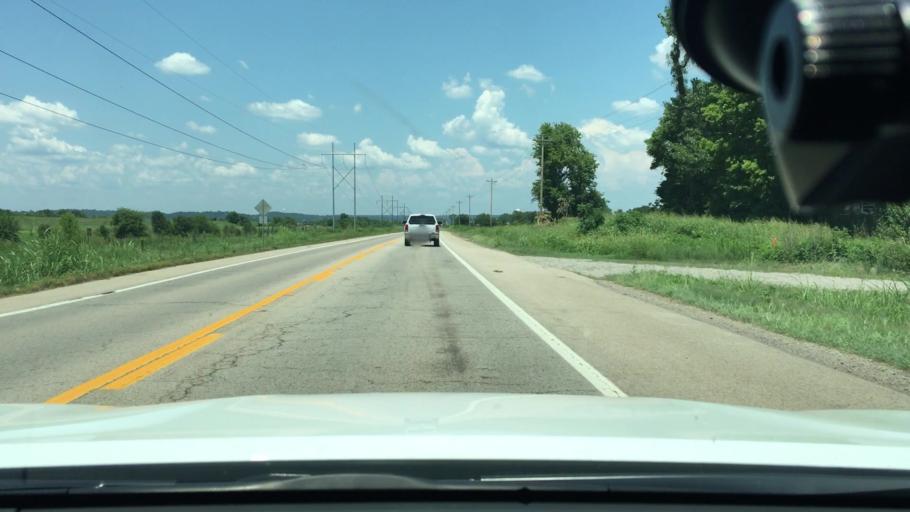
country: US
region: Arkansas
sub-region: Crawford County
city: Van Buren
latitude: 35.3947
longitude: -94.3304
